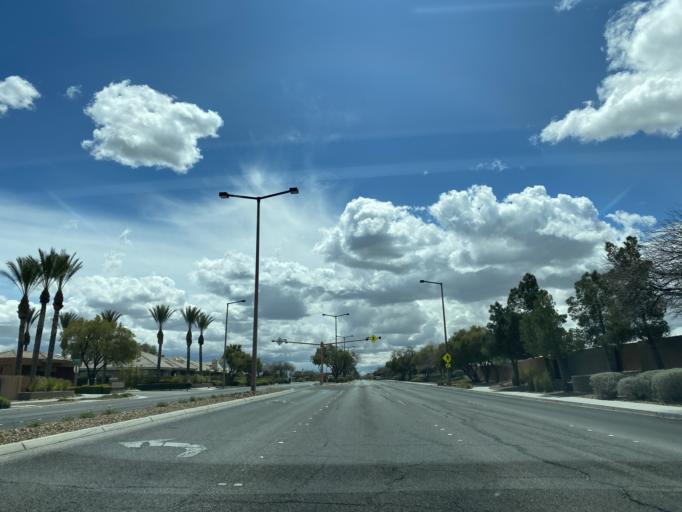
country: US
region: Nevada
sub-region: Clark County
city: Summerlin South
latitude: 36.1756
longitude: -115.3163
